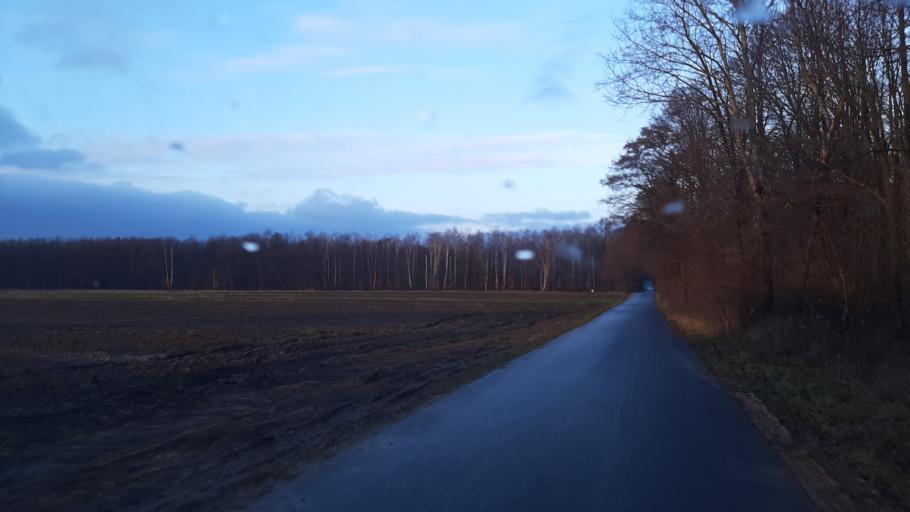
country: PL
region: Lublin Voivodeship
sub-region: Powiat lubelski
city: Garbow
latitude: 51.3716
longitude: 22.3995
